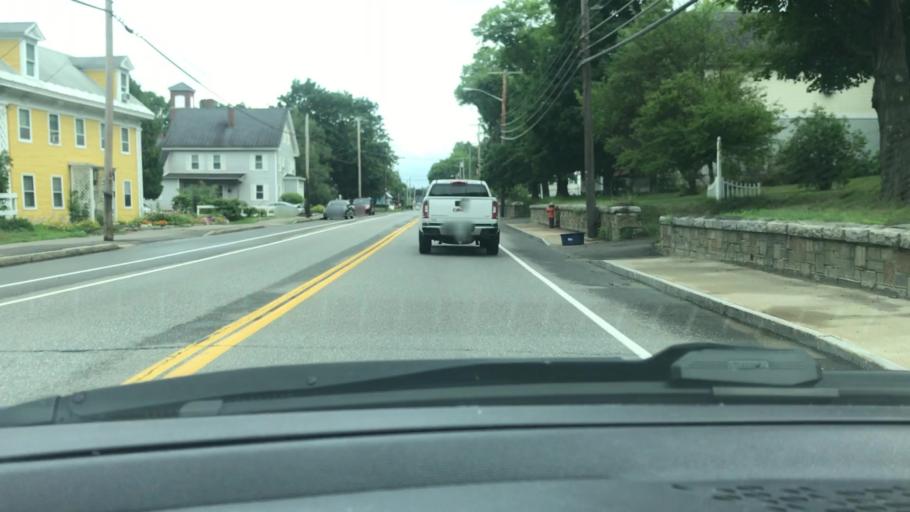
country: US
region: New Hampshire
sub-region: Merrimack County
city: East Concord
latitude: 43.2427
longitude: -71.5702
